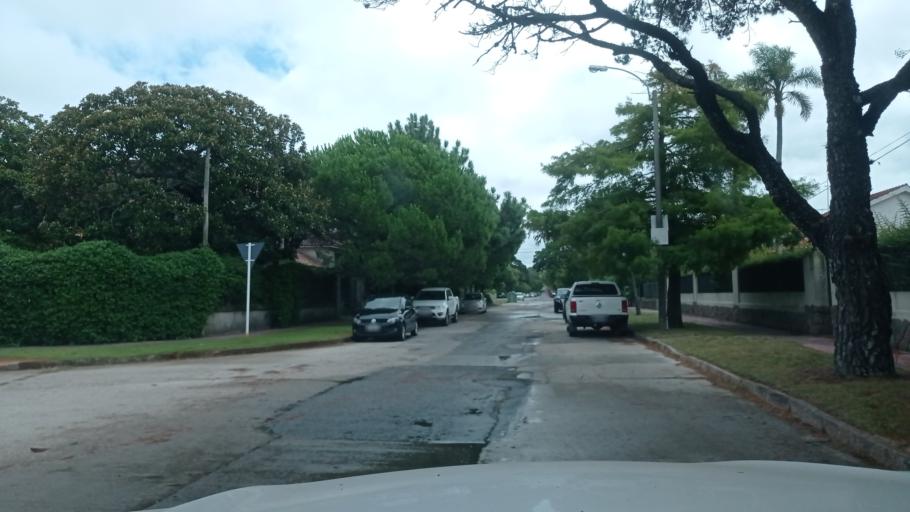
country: UY
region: Canelones
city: Barra de Carrasco
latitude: -34.8885
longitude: -56.0541
